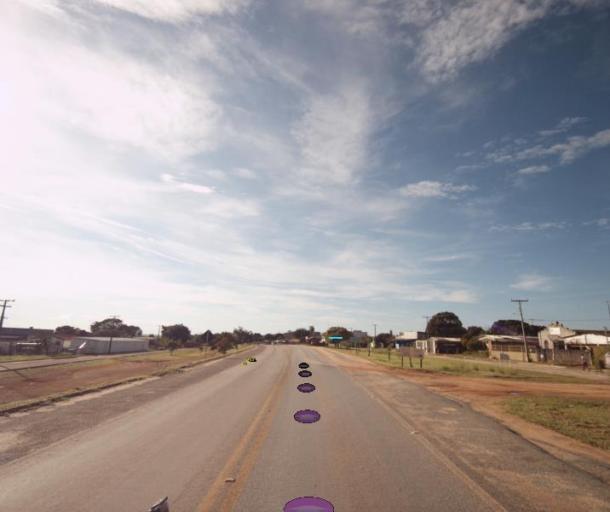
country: BR
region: Goias
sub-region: Pirenopolis
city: Pirenopolis
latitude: -15.7781
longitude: -48.5375
